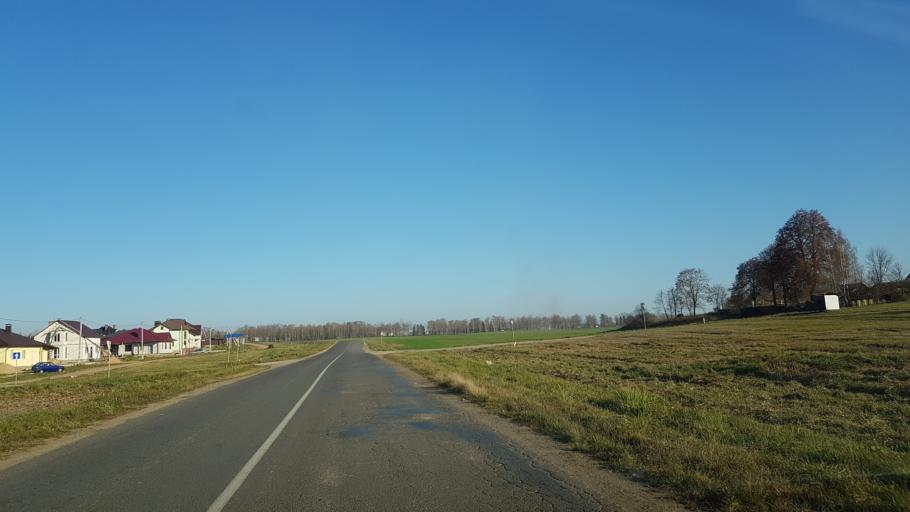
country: BY
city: Fanipol
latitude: 53.7247
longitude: 27.3214
